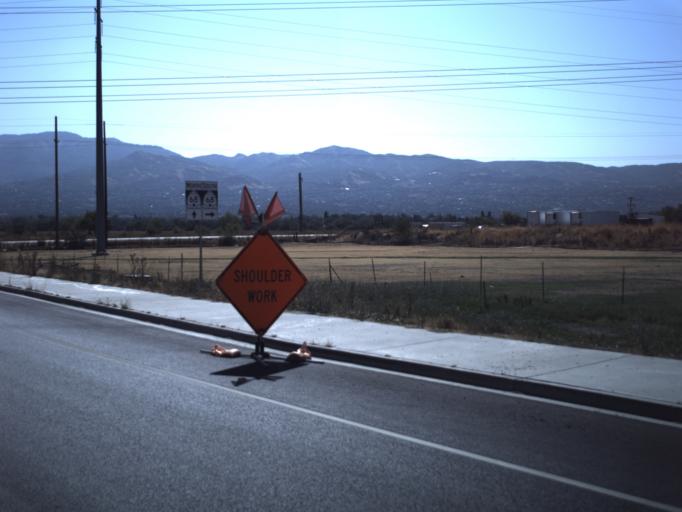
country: US
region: Utah
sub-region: Davis County
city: West Bountiful
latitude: 40.8840
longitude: -111.9316
